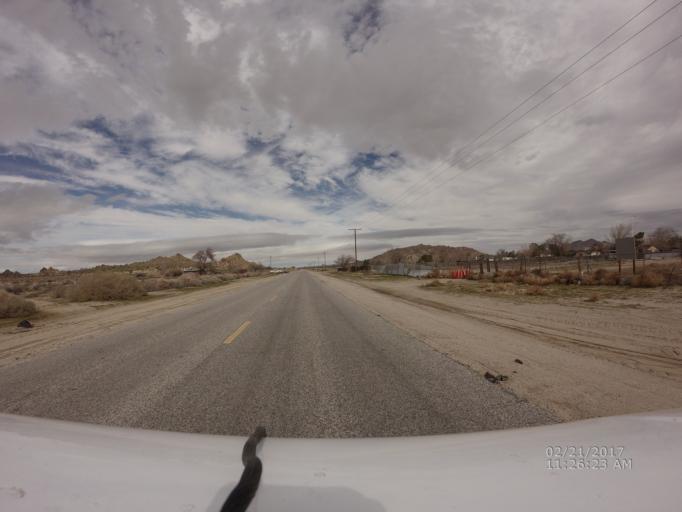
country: US
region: California
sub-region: Los Angeles County
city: Lake Los Angeles
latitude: 34.6337
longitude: -117.8629
